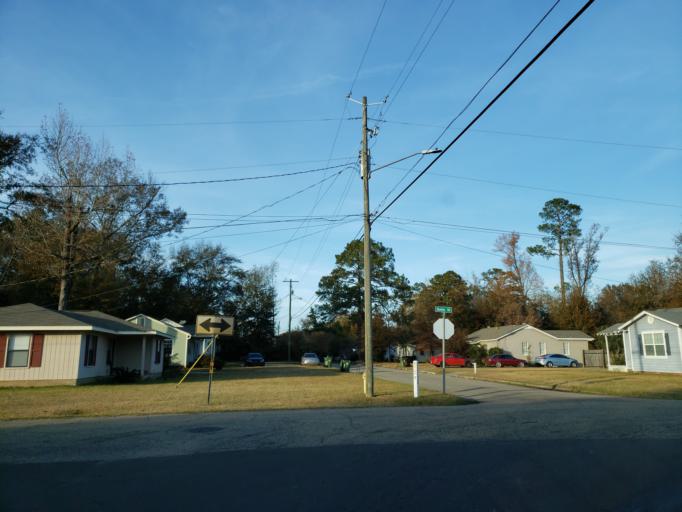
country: US
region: Mississippi
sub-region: Forrest County
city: Hattiesburg
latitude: 31.3283
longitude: -89.3192
